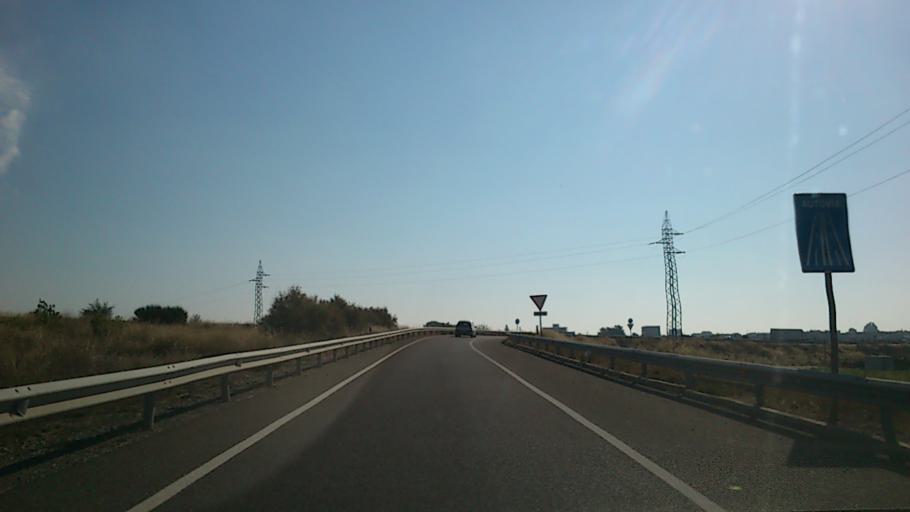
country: ES
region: Aragon
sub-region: Provincia de Zaragoza
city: Zaragoza
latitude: 41.6924
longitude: -0.8365
